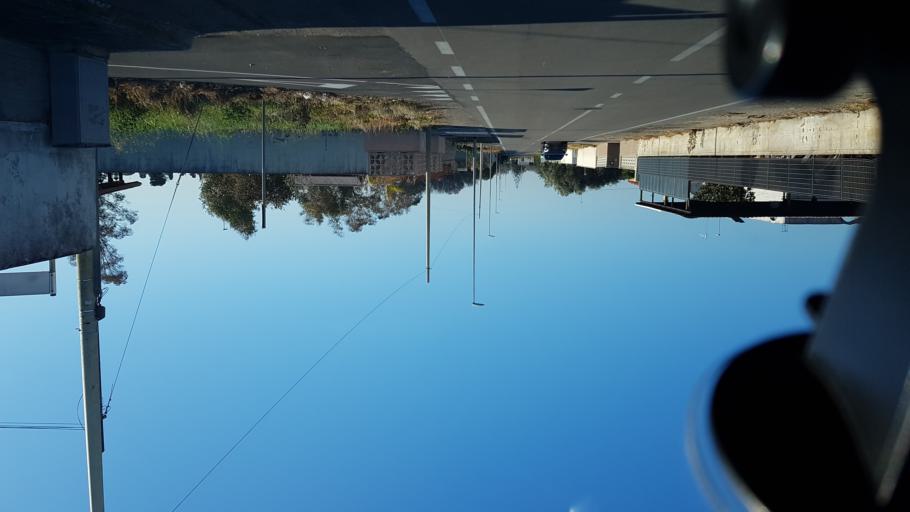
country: IT
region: Apulia
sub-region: Provincia di Lecce
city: Merine
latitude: 40.4306
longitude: 18.2422
